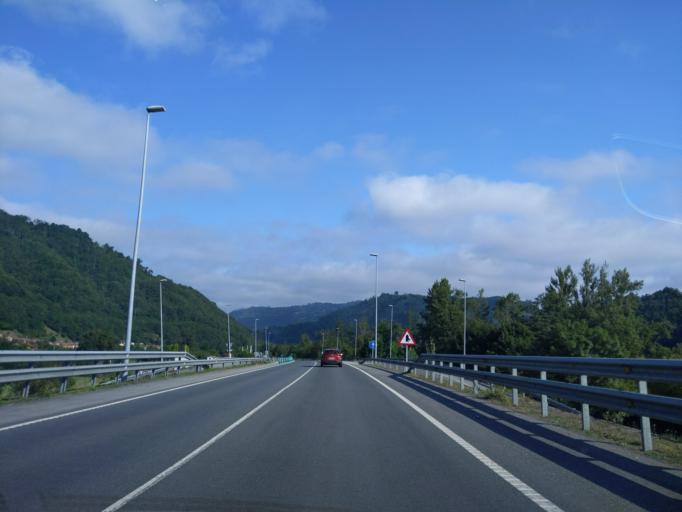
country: ES
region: Asturias
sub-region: Province of Asturias
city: Pola de Laviana
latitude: 43.2500
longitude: -5.5686
